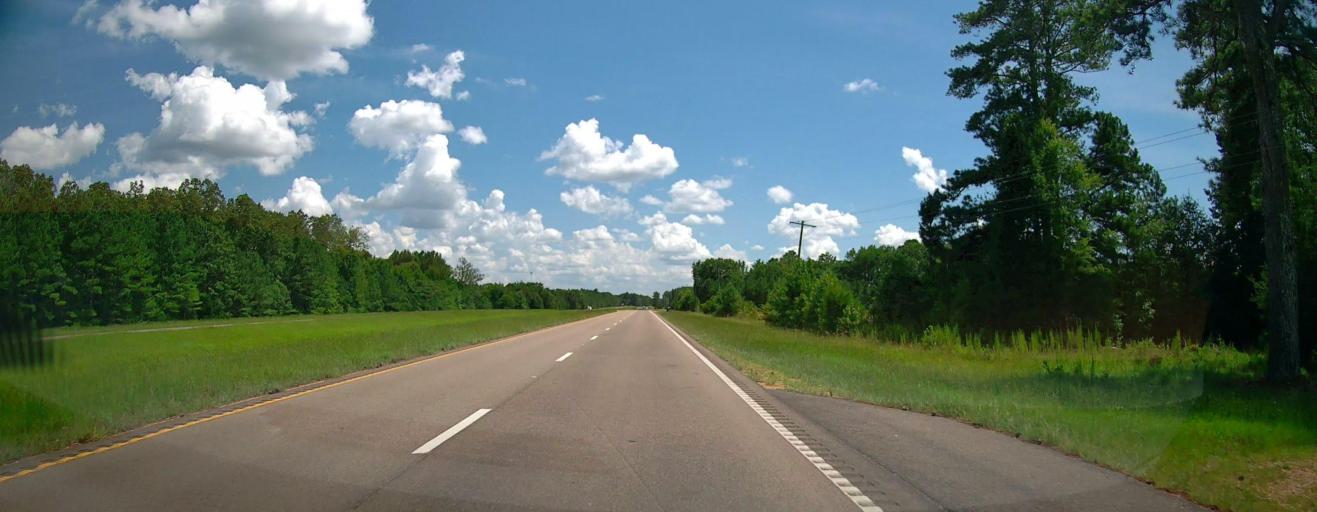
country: US
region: Mississippi
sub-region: Monroe County
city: Amory
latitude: 33.9384
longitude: -88.5978
